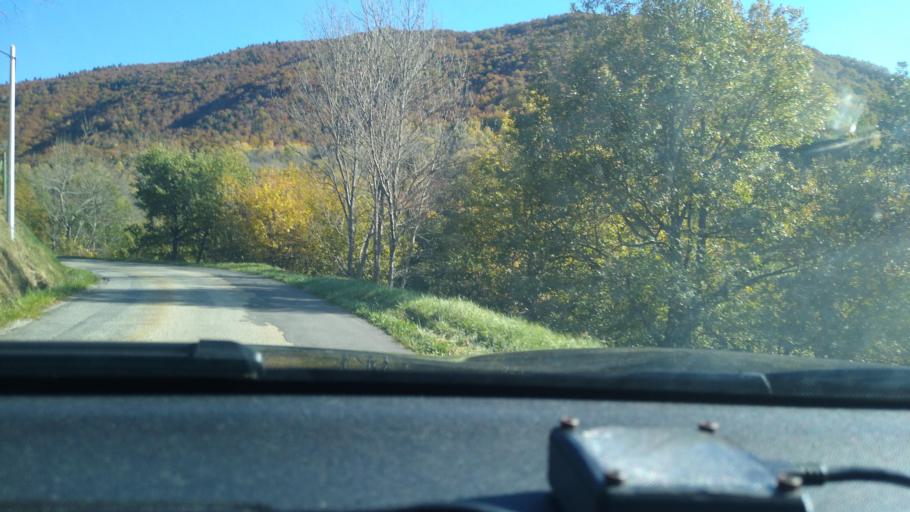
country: FR
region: Midi-Pyrenees
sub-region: Departement de l'Ariege
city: Ax-les-Thermes
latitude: 42.7197
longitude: 1.8695
